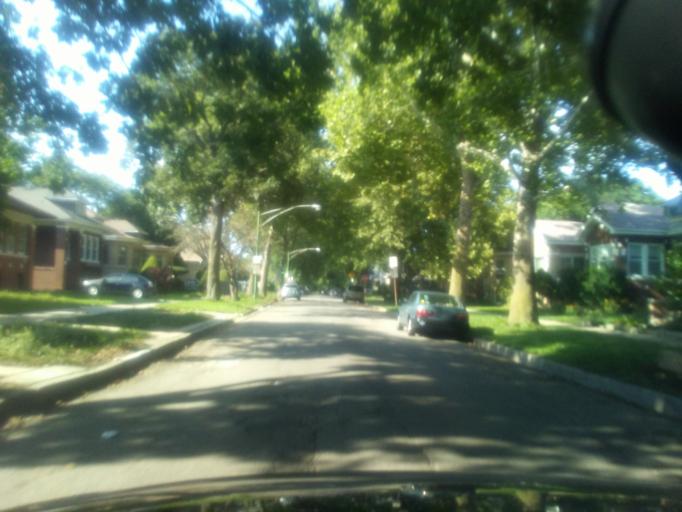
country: US
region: Illinois
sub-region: Cook County
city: Lincolnwood
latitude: 41.9712
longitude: -87.7232
